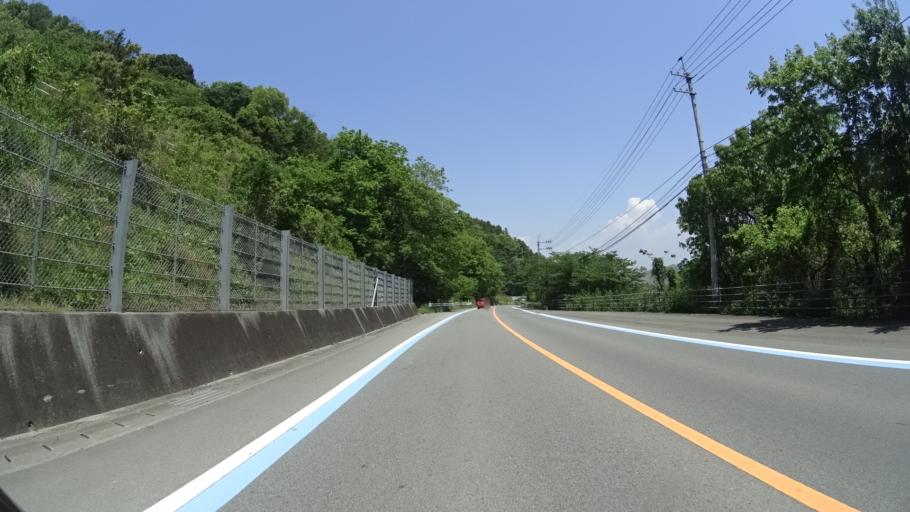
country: JP
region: Ehime
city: Iyo
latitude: 33.7210
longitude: 132.6786
